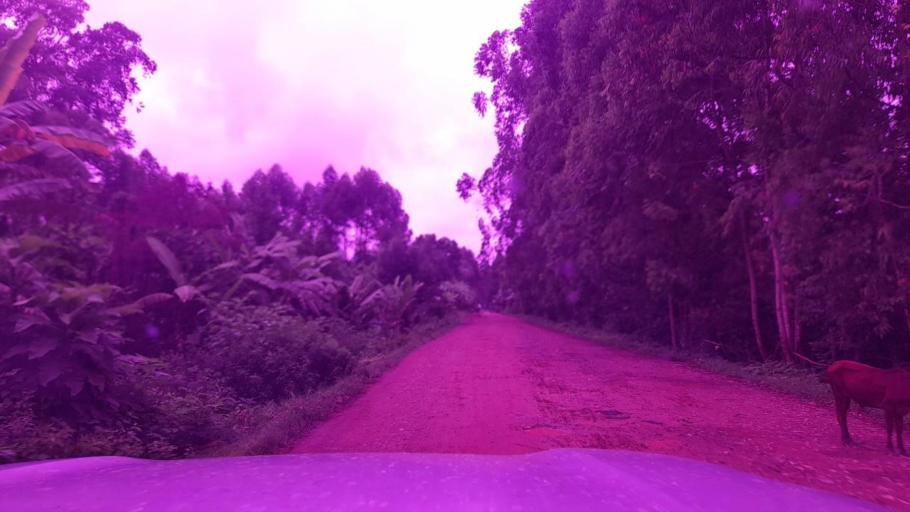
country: ET
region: Southern Nations, Nationalities, and People's Region
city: Bonga
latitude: 7.5786
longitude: 36.0331
